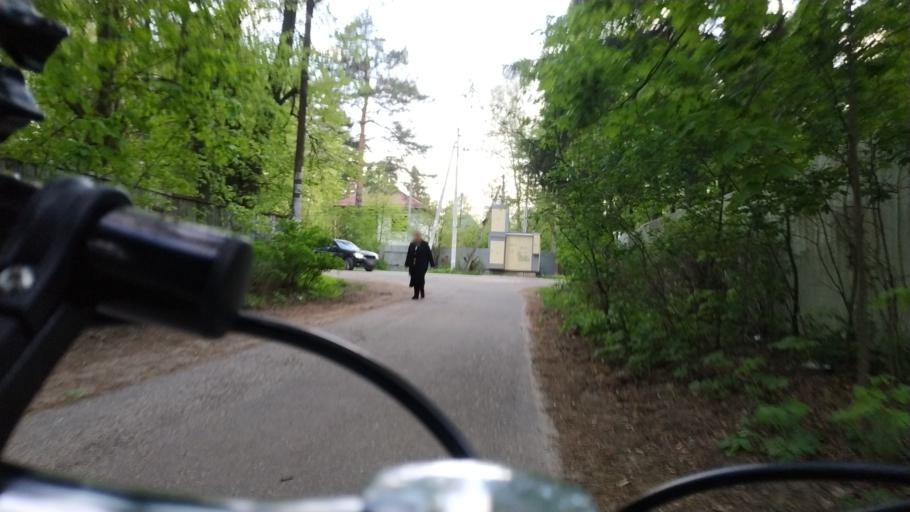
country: RU
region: Moskovskaya
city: Kratovo
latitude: 55.5943
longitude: 38.1618
